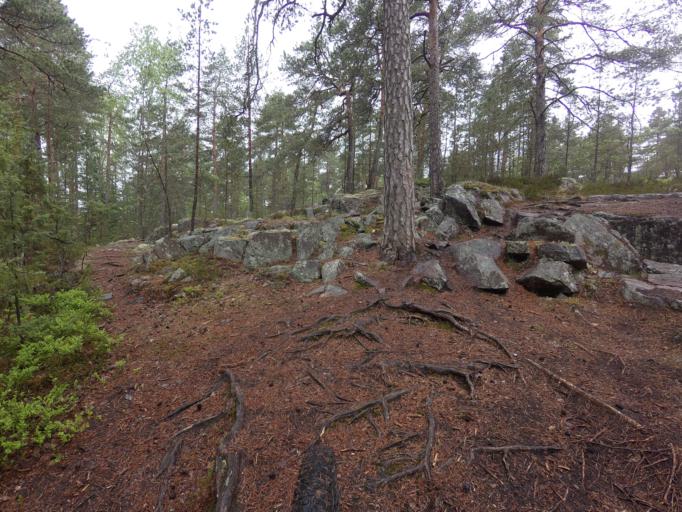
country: FI
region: Uusimaa
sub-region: Helsinki
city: Kauniainen
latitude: 60.1852
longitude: 24.6988
